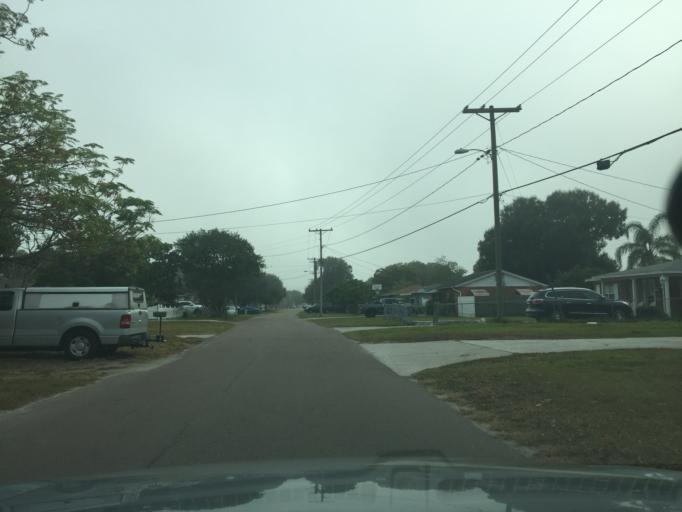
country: US
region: Florida
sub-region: Hillsborough County
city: Tampa
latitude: 27.9542
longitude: -82.4887
